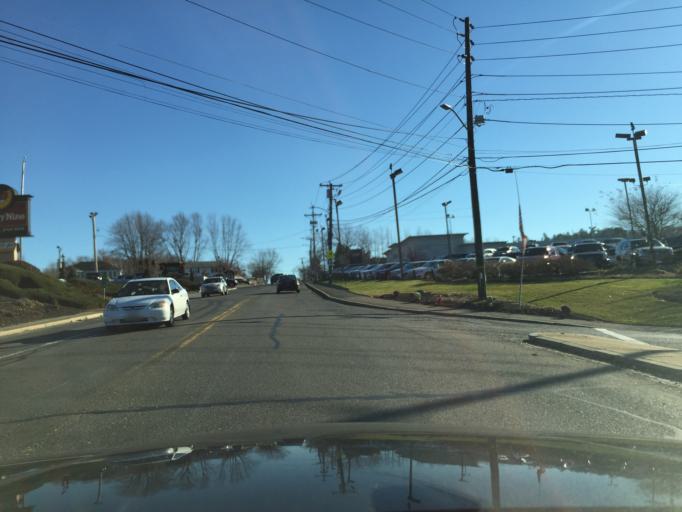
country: US
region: Massachusetts
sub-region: Middlesex County
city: Woburn
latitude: 42.4673
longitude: -71.1778
